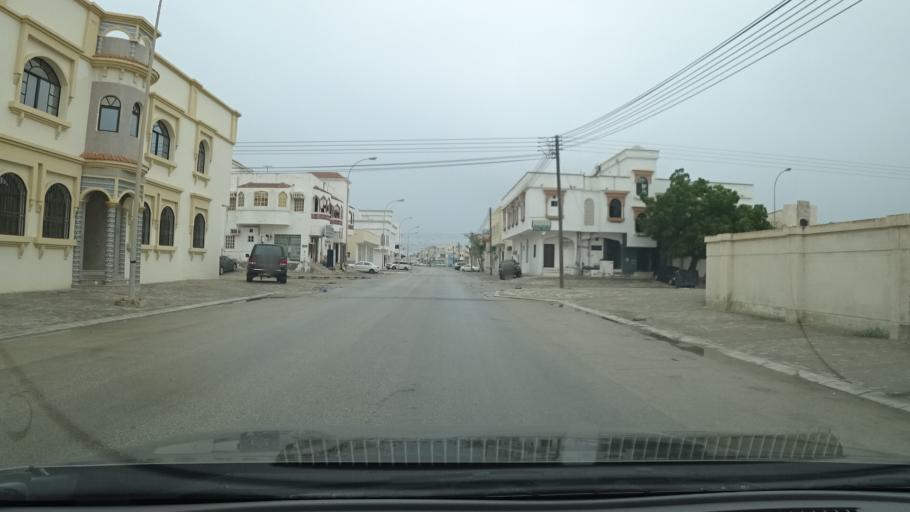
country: OM
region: Zufar
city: Salalah
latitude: 17.0240
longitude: 54.1589
